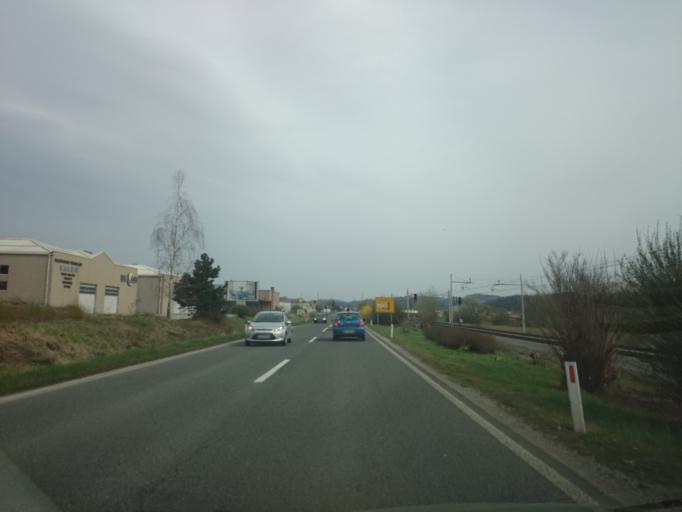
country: SI
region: Sentjur pri Celju
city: Sentjur
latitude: 46.2140
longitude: 15.3864
